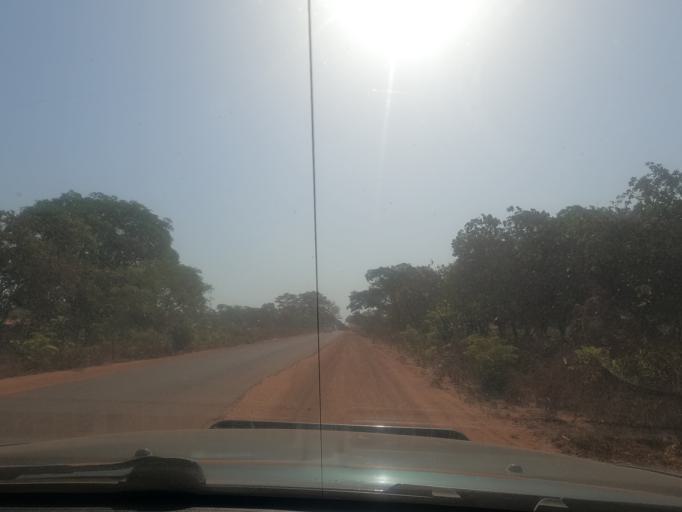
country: GW
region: Oio
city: Mansoa
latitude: 12.0044
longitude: -15.4237
